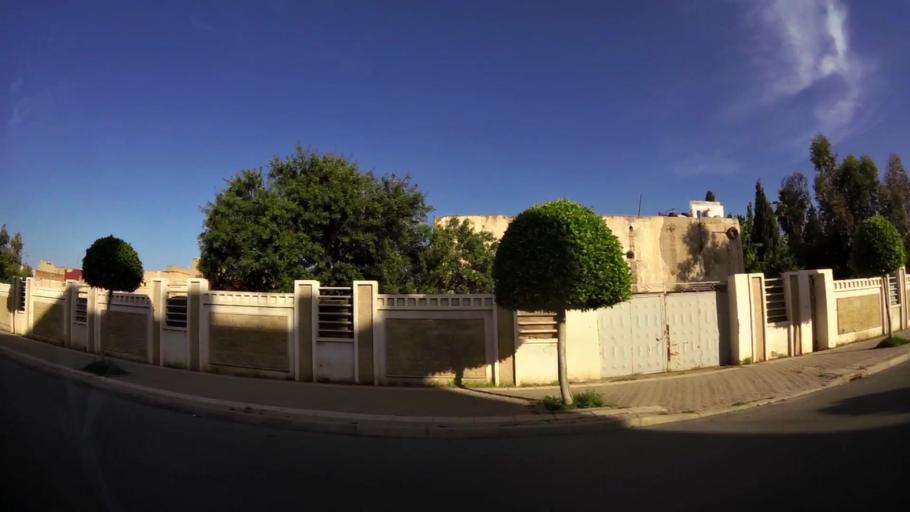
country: MA
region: Oriental
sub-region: Oujda-Angad
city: Oujda
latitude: 34.6976
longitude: -1.9007
